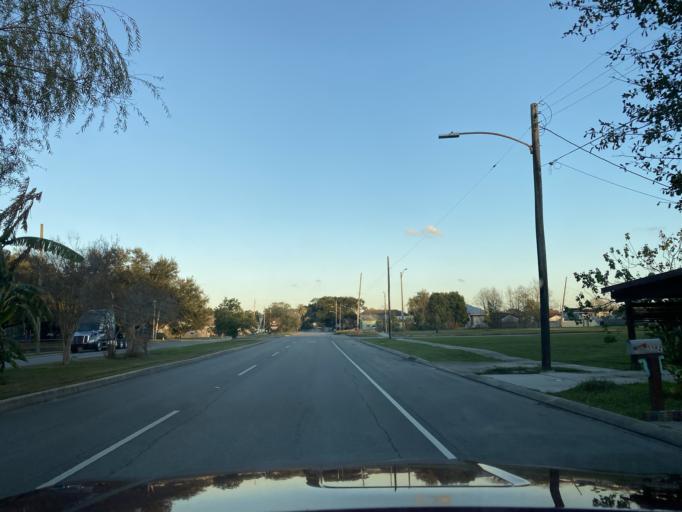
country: US
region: Louisiana
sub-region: Orleans Parish
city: New Orleans
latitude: 30.0222
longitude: -90.0573
